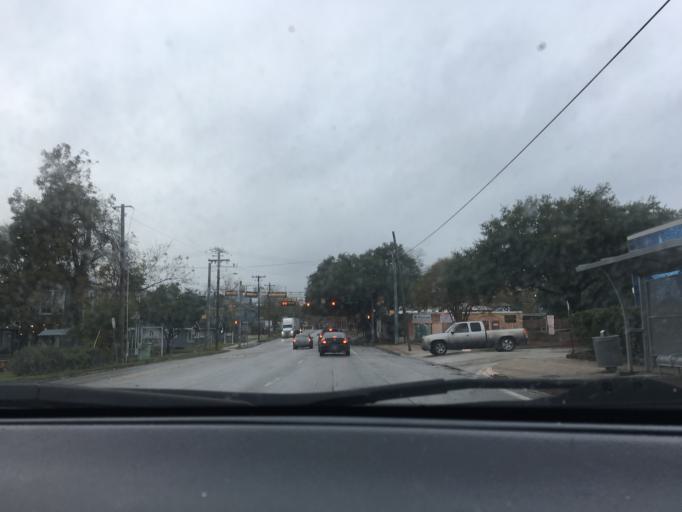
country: US
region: Texas
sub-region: Hays County
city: San Marcos
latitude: 29.8829
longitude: -97.9431
